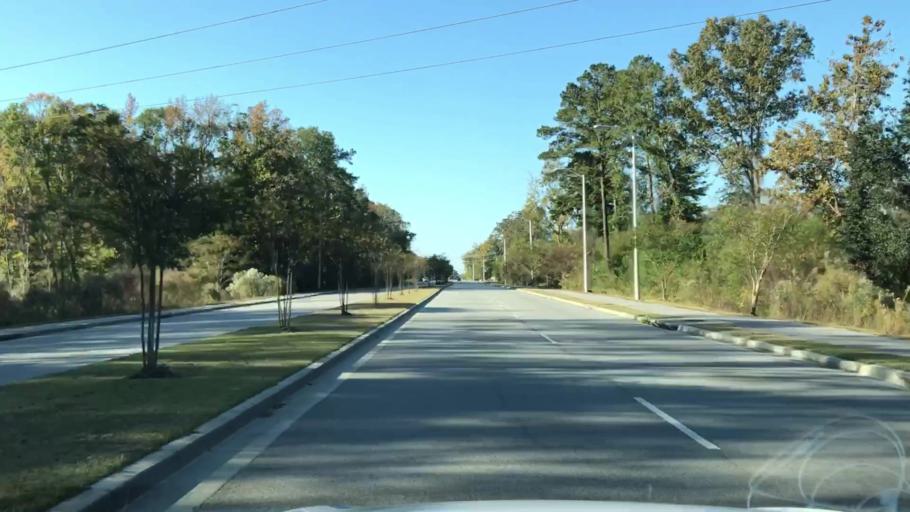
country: US
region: South Carolina
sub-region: Charleston County
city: Shell Point
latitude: 32.8137
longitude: -80.1030
